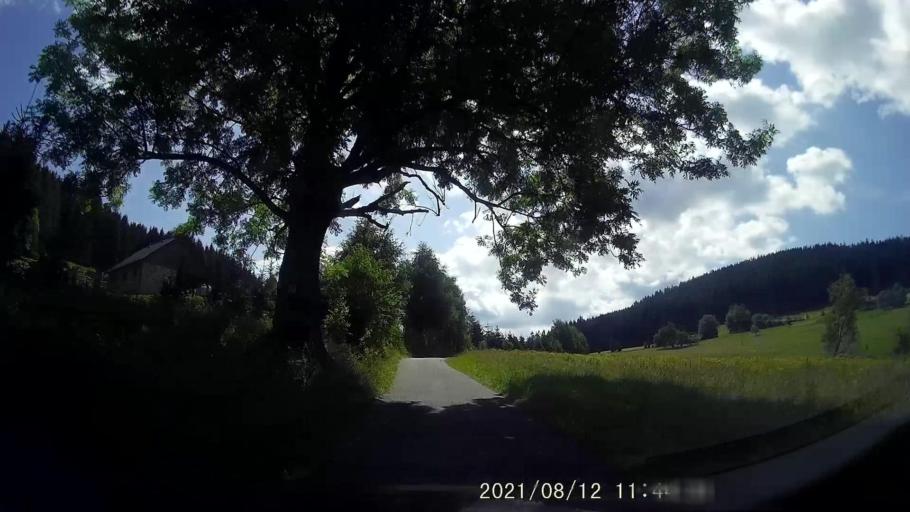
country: PL
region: Lower Silesian Voivodeship
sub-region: Powiat klodzki
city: Stronie Slaskie
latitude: 50.2568
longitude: 16.8362
